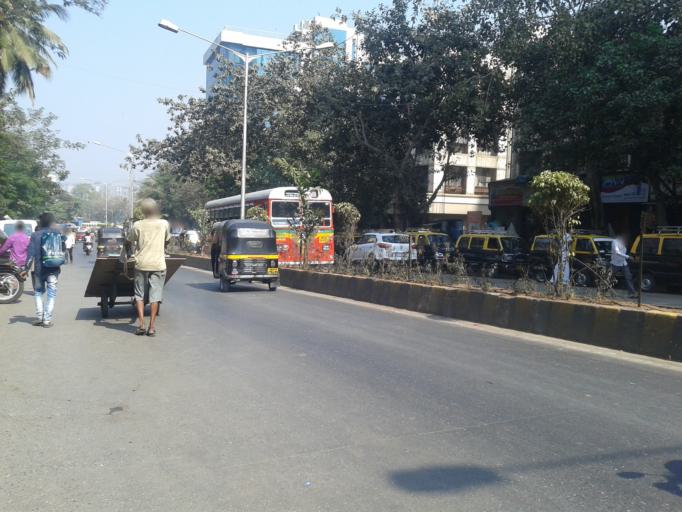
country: IN
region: Maharashtra
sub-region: Mumbai Suburban
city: Borivli
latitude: 19.2526
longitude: 72.8644
